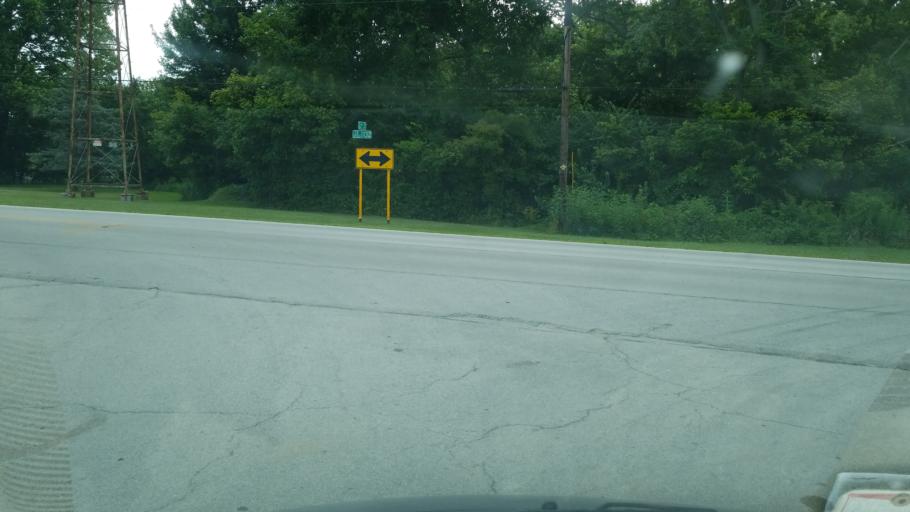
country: US
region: Ohio
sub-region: Sandusky County
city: Ballville
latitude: 41.2987
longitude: -83.1641
